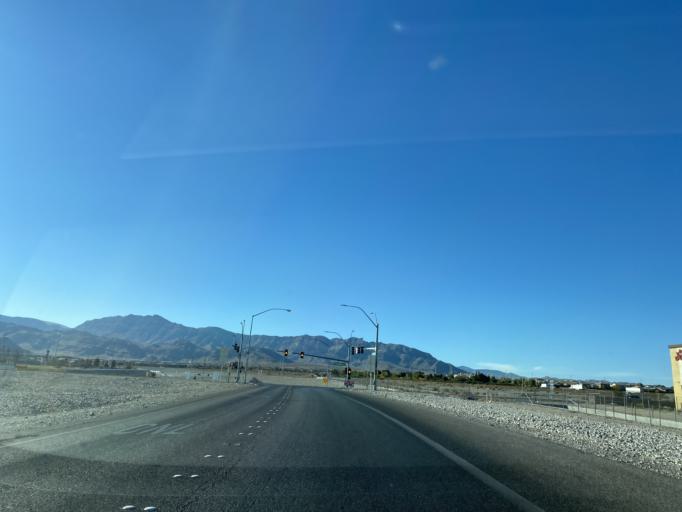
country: US
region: Nevada
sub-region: Clark County
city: Summerlin South
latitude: 36.2833
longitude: -115.3138
